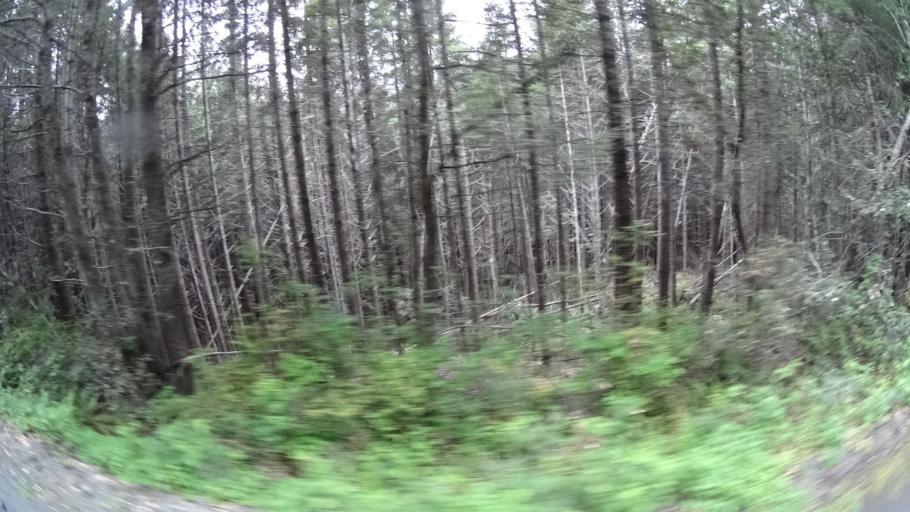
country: US
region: California
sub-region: Humboldt County
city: Willow Creek
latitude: 41.2003
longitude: -123.7599
